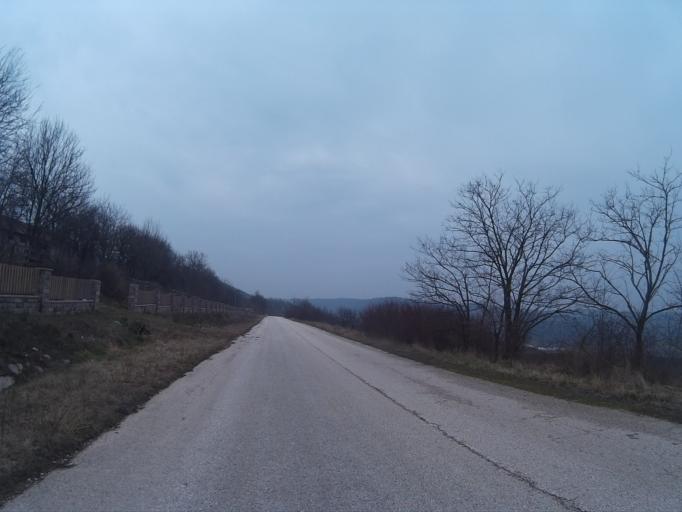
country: HU
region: Fejer
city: Many
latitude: 47.5328
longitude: 18.6024
